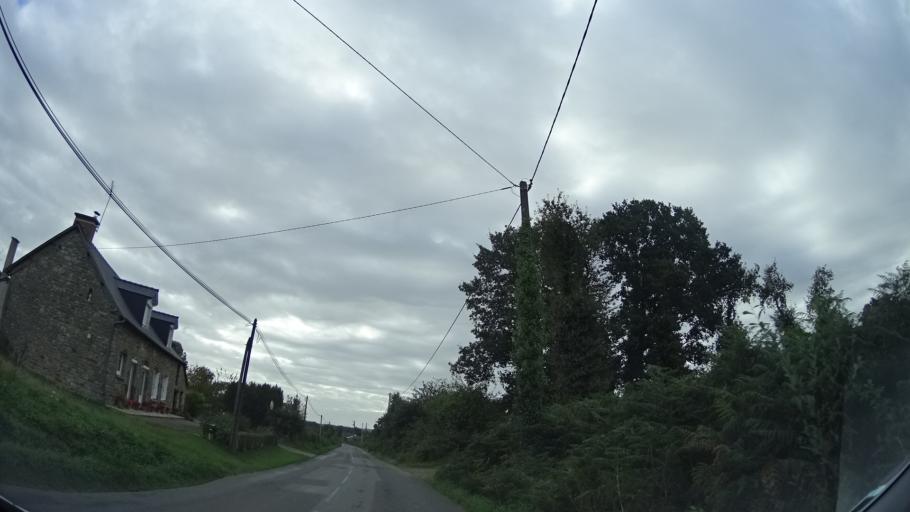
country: FR
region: Brittany
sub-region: Departement d'Ille-et-Vilaine
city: Dinge
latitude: 48.3560
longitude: -1.7078
